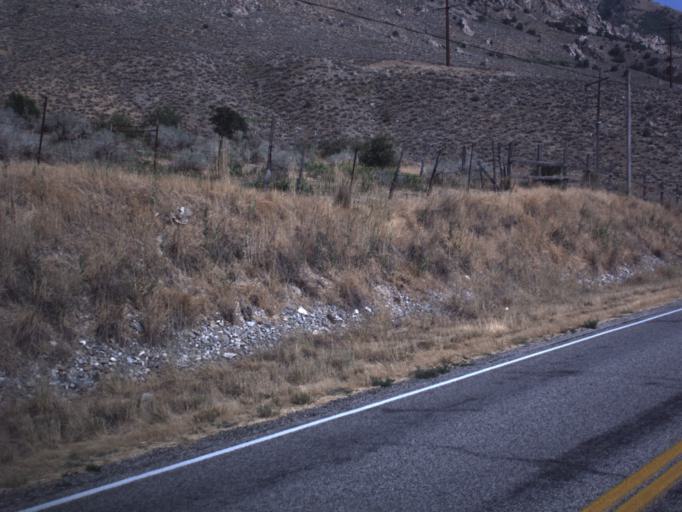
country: US
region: Utah
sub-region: Box Elder County
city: Brigham City
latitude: 41.5583
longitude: -112.0220
